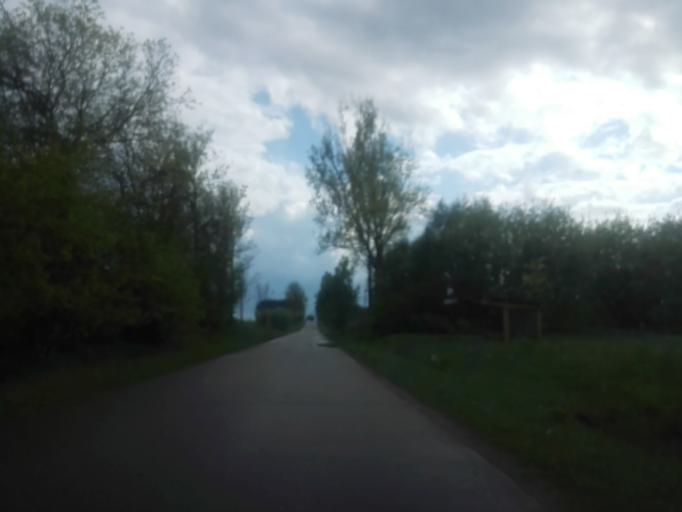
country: PL
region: Podlasie
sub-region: Powiat lomzynski
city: Wizna
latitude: 53.2636
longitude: 22.4489
